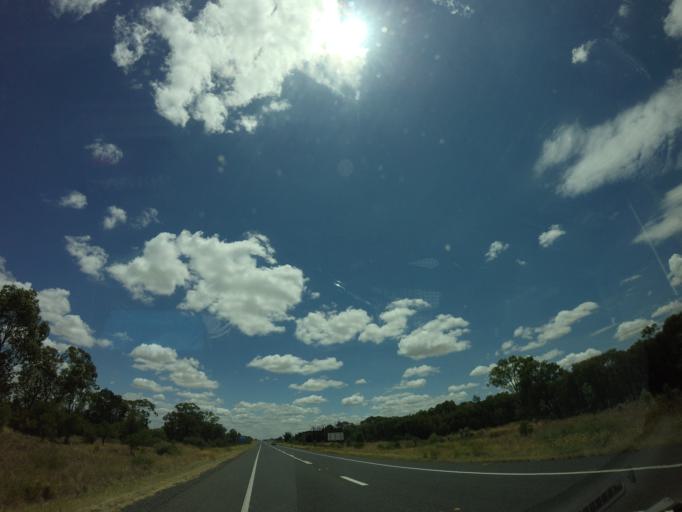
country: AU
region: New South Wales
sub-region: Moree Plains
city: Boggabilla
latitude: -28.8447
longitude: 150.2234
